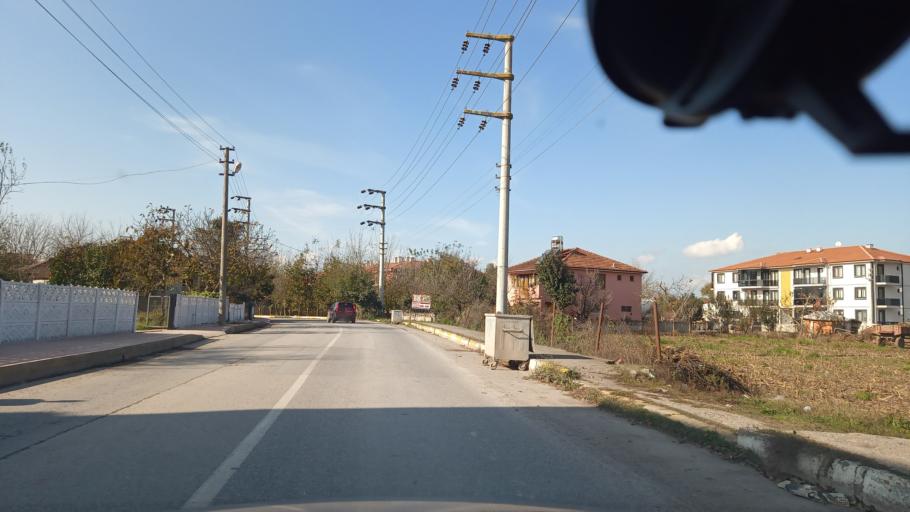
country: TR
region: Sakarya
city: Sogutlu
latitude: 40.8795
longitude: 30.4652
